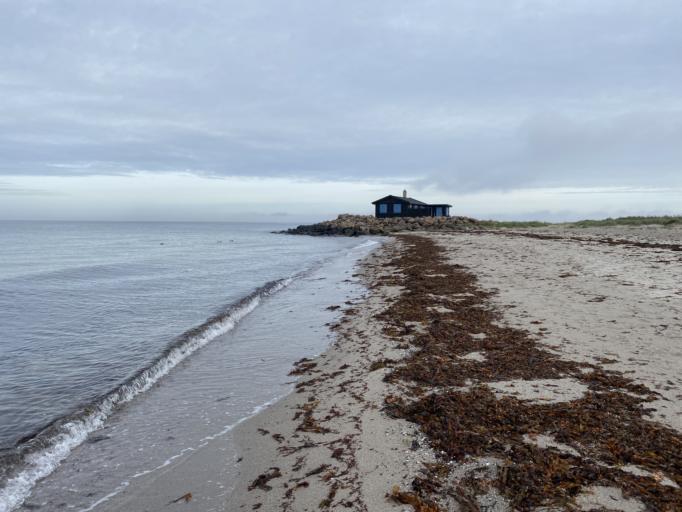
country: DK
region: Zealand
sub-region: Odsherred Kommune
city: Nykobing Sjaelland
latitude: 55.9698
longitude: 11.7526
